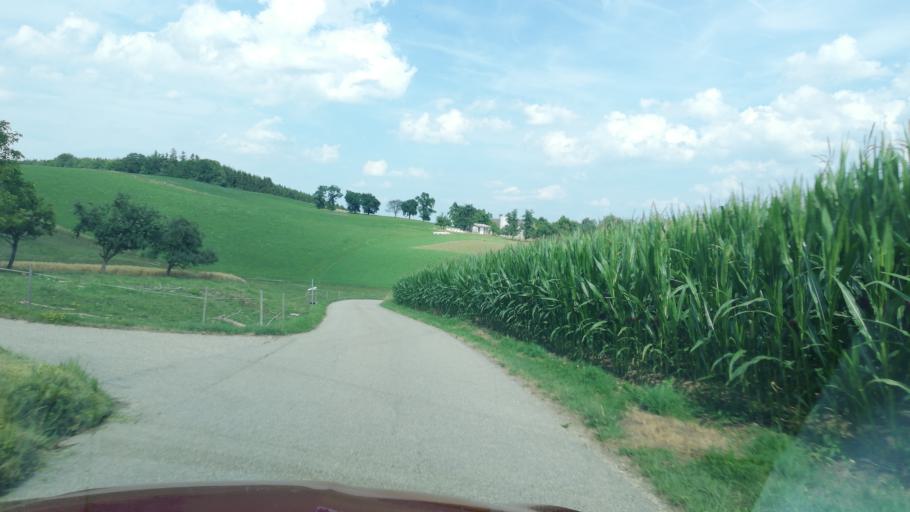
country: AT
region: Upper Austria
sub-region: Politischer Bezirk Vocklabruck
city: Puhret
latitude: 48.0360
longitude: 13.7291
